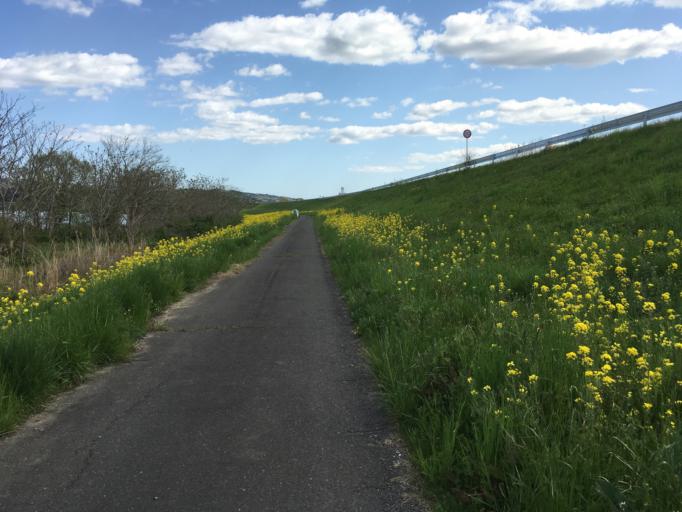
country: JP
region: Miyagi
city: Wakuya
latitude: 38.7127
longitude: 141.2654
